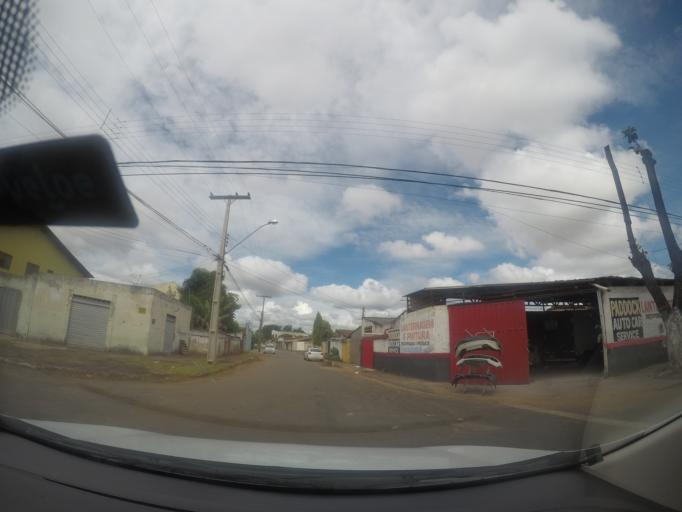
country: BR
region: Goias
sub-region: Goiania
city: Goiania
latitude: -16.6578
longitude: -49.3023
